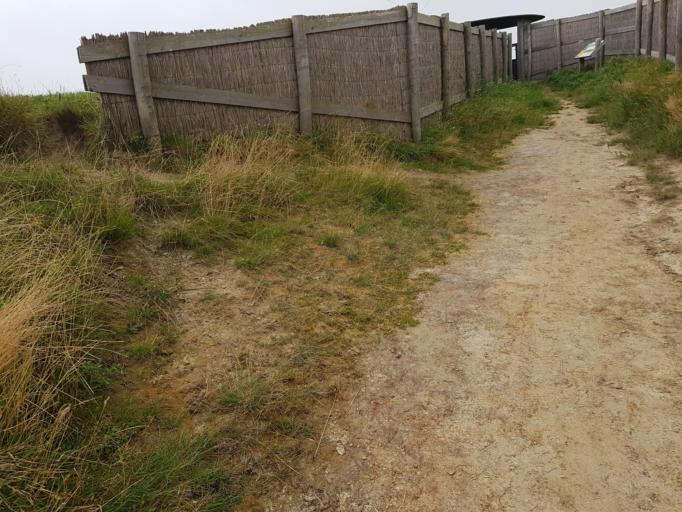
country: NL
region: North Holland
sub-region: Gemeente Texel
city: Den Burg
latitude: 53.0606
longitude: 4.8665
